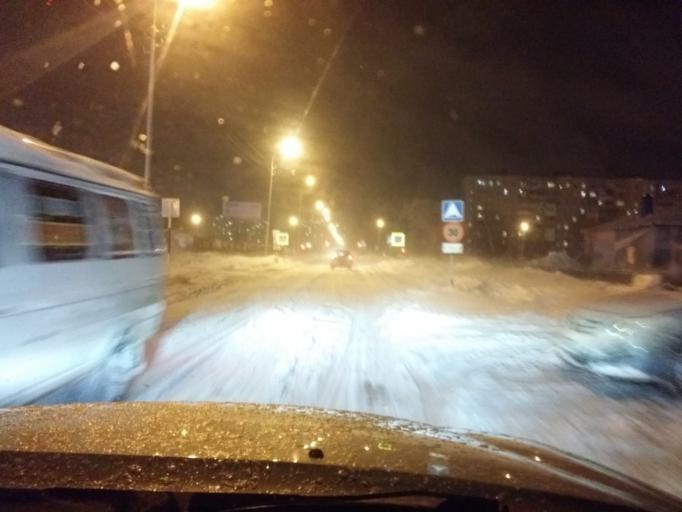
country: RU
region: Khanty-Mansiyskiy Avtonomnyy Okrug
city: Nizhnevartovsk
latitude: 60.9411
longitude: 76.5948
